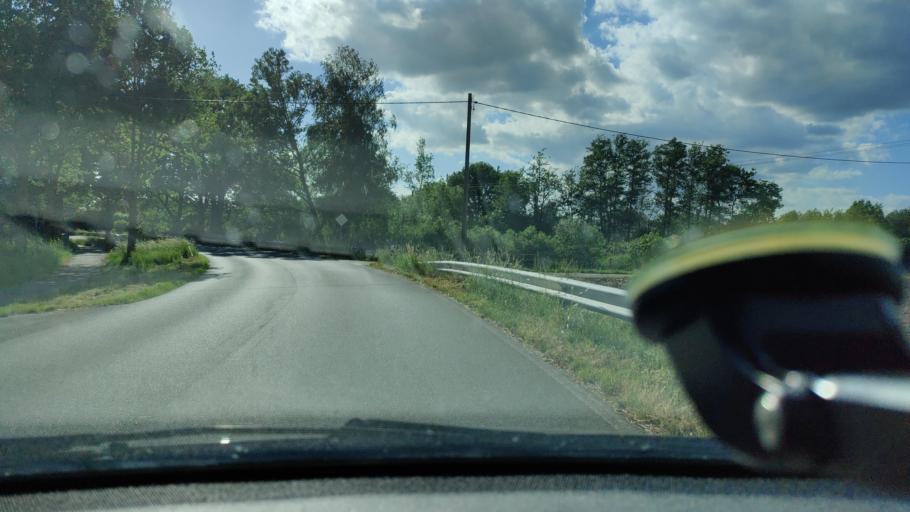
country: DE
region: North Rhine-Westphalia
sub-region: Regierungsbezirk Munster
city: Heiden
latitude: 51.8917
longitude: 6.9244
